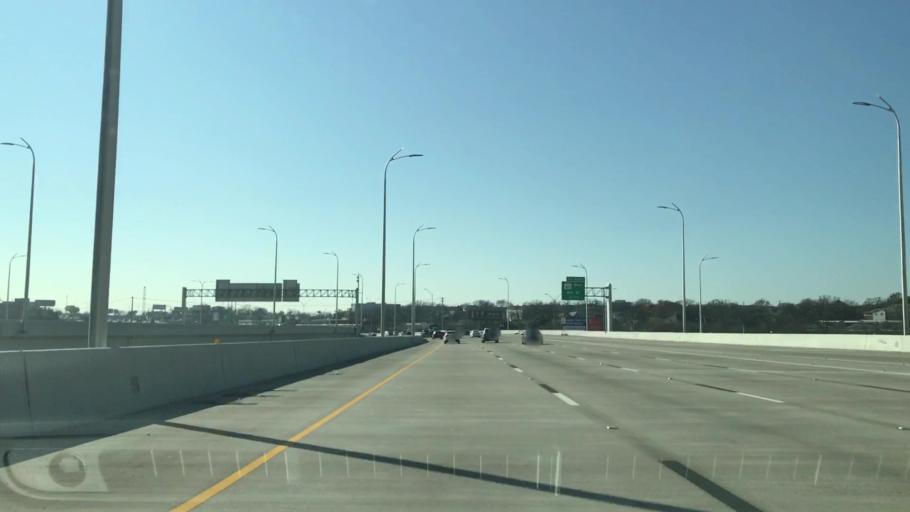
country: US
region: Texas
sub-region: Dallas County
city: Dallas
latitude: 32.7602
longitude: -96.8090
